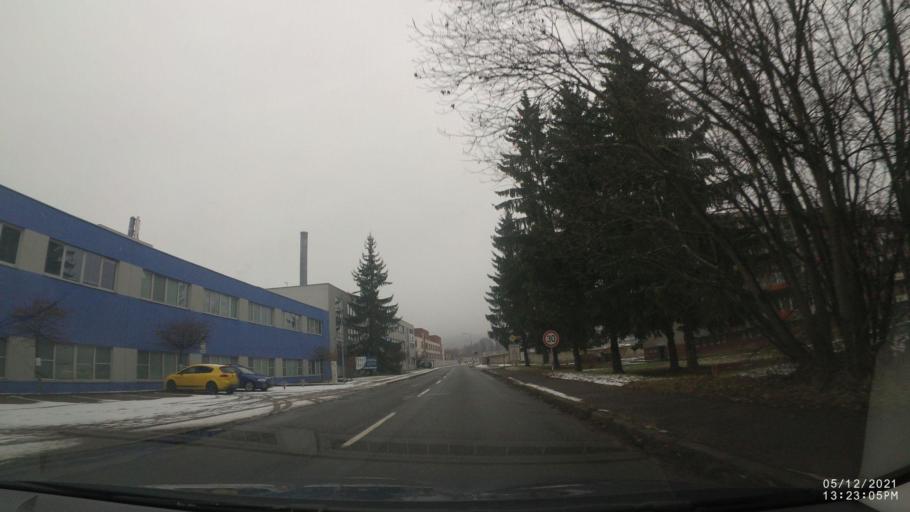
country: CZ
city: Hronov
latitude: 50.4690
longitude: 16.1804
